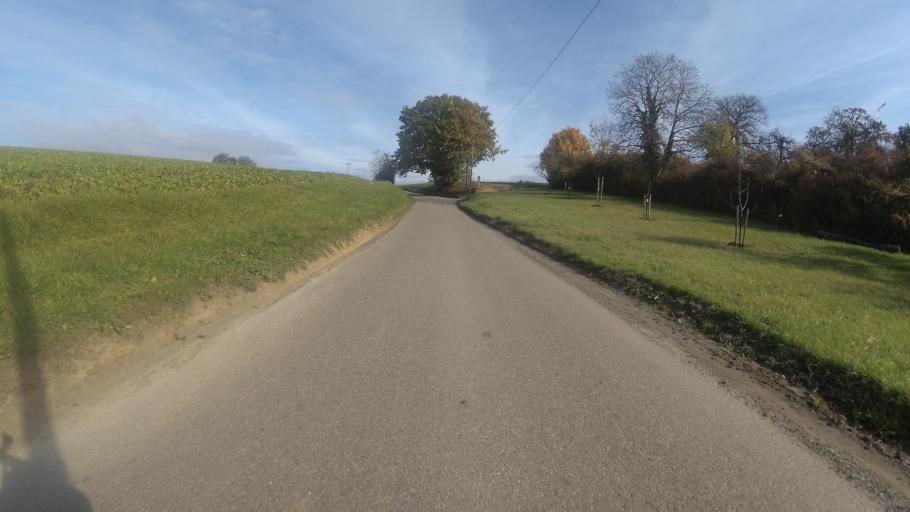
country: DE
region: Baden-Wuerttemberg
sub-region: Regierungsbezirk Stuttgart
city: Oedheim
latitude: 49.2605
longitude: 9.2662
